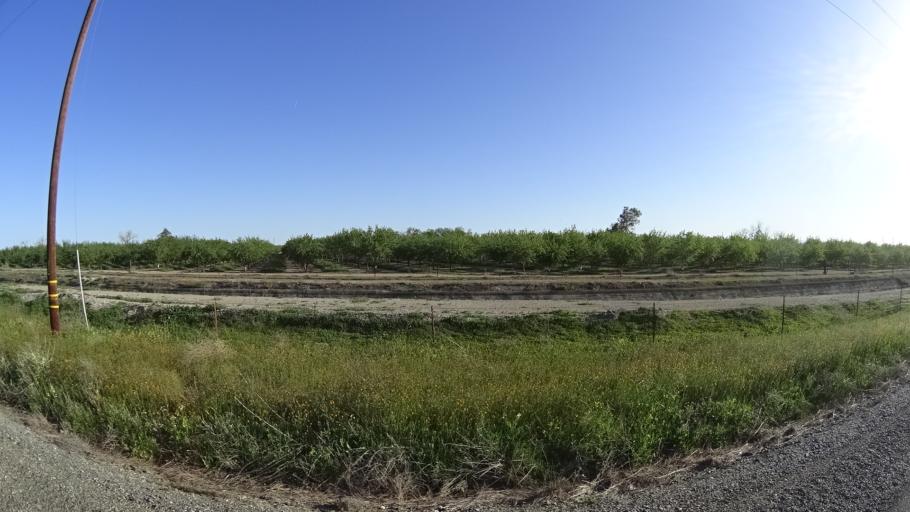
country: US
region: California
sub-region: Glenn County
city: Orland
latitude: 39.7799
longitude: -122.2884
